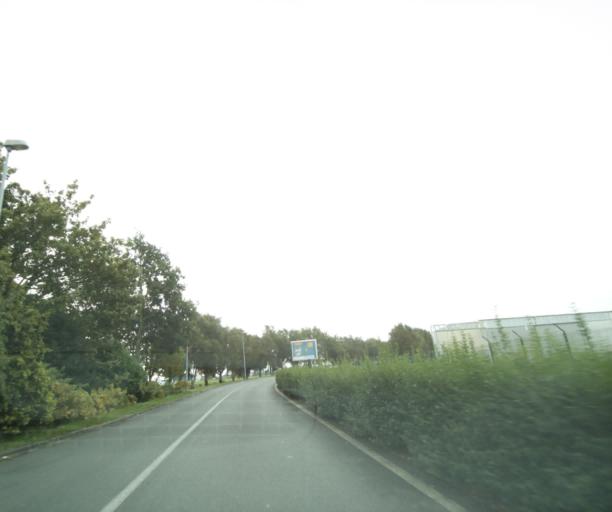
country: FR
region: Nord-Pas-de-Calais
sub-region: Departement du Nord
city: Vendeville
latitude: 50.5736
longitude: 3.0967
